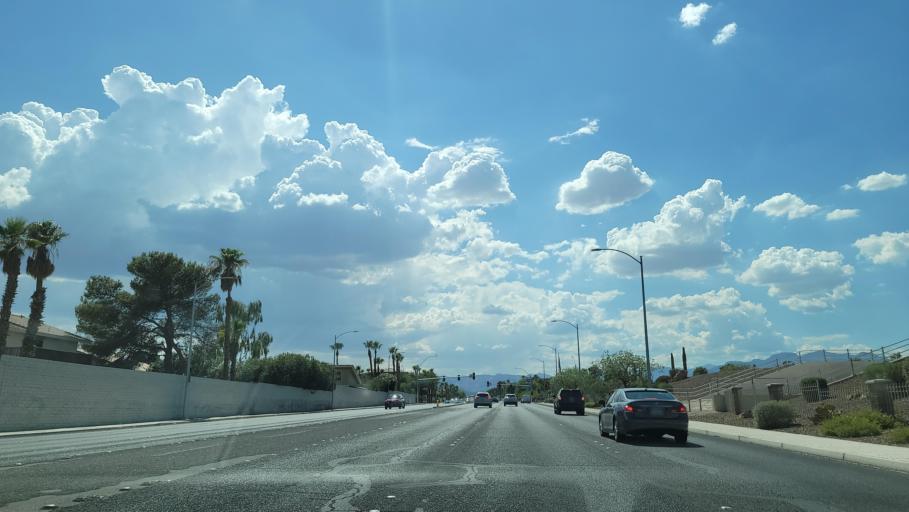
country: US
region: Nevada
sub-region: Clark County
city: Spring Valley
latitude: 36.1295
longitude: -115.2407
